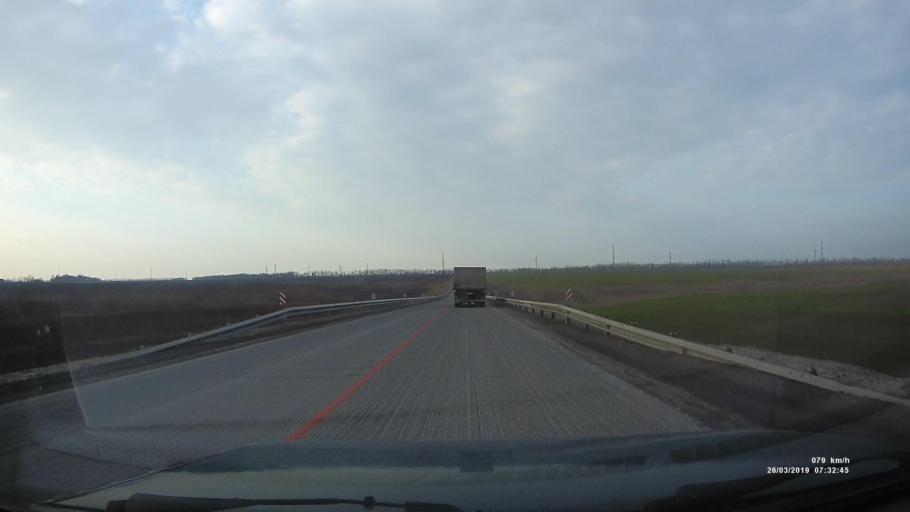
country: RU
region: Rostov
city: Novobessergenovka
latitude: 47.2217
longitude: 38.7749
